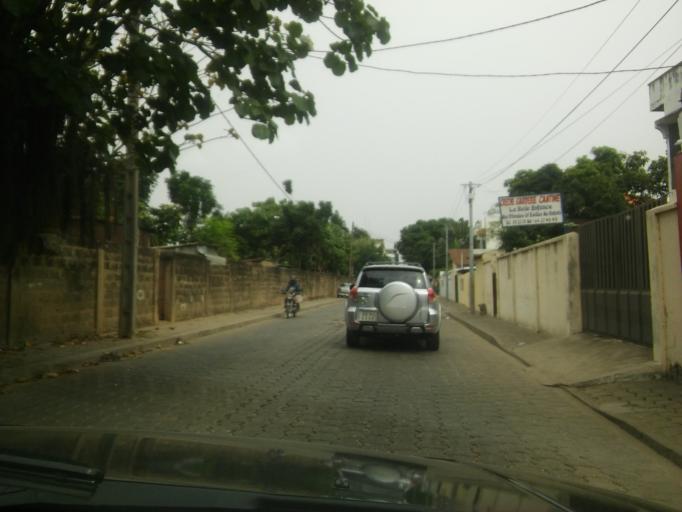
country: BJ
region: Littoral
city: Cotonou
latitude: 6.3563
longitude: 2.4191
